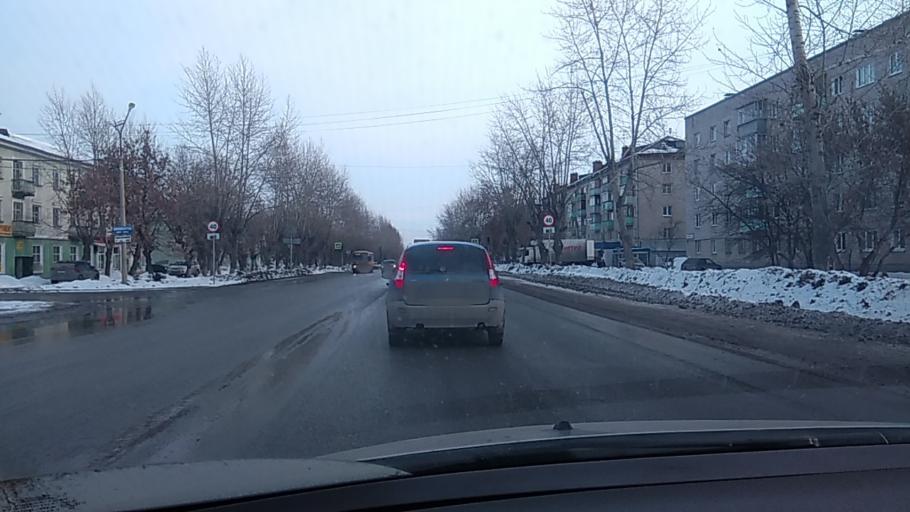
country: RU
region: Sverdlovsk
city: Martyush
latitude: 56.4355
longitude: 61.8460
